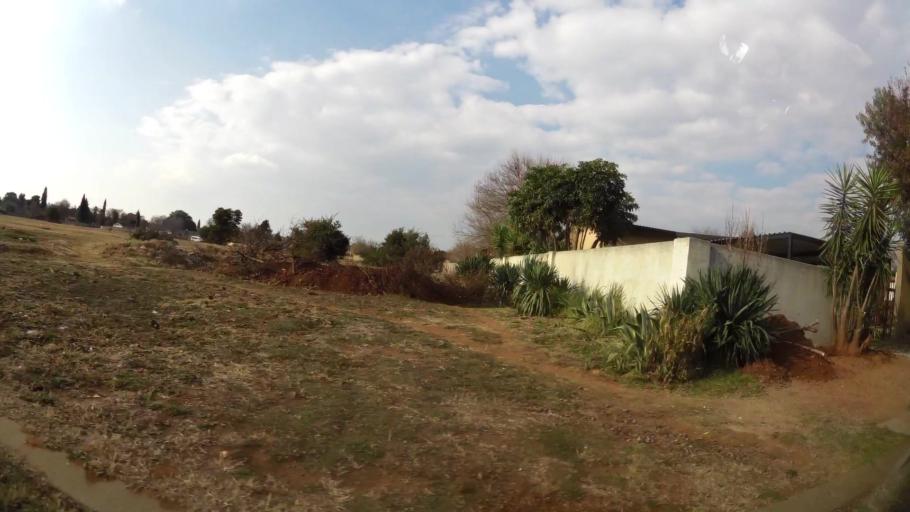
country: ZA
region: Gauteng
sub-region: Ekurhuleni Metropolitan Municipality
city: Benoni
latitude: -26.1214
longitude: 28.3704
